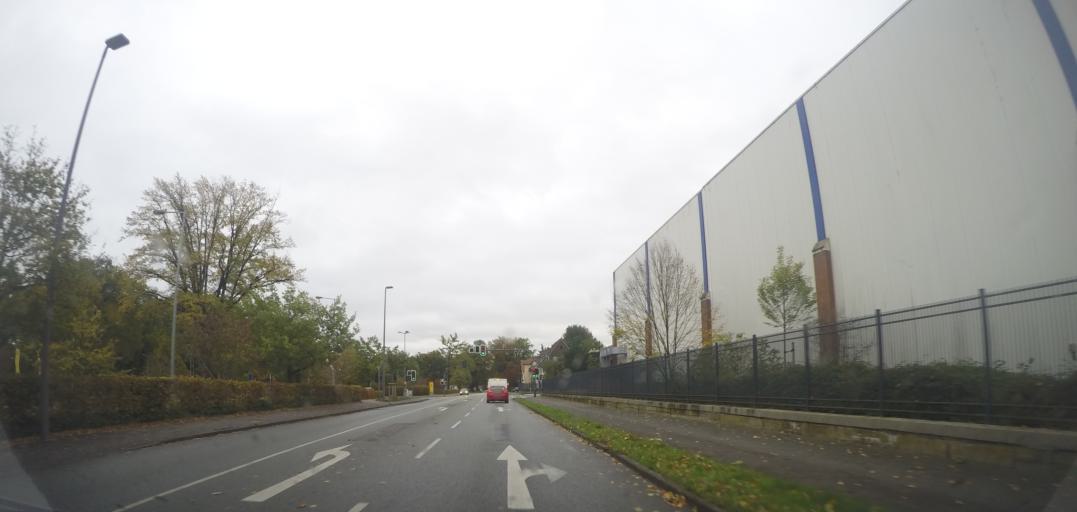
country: DE
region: North Rhine-Westphalia
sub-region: Regierungsbezirk Arnsberg
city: Lippstadt
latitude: 51.6792
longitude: 8.3199
